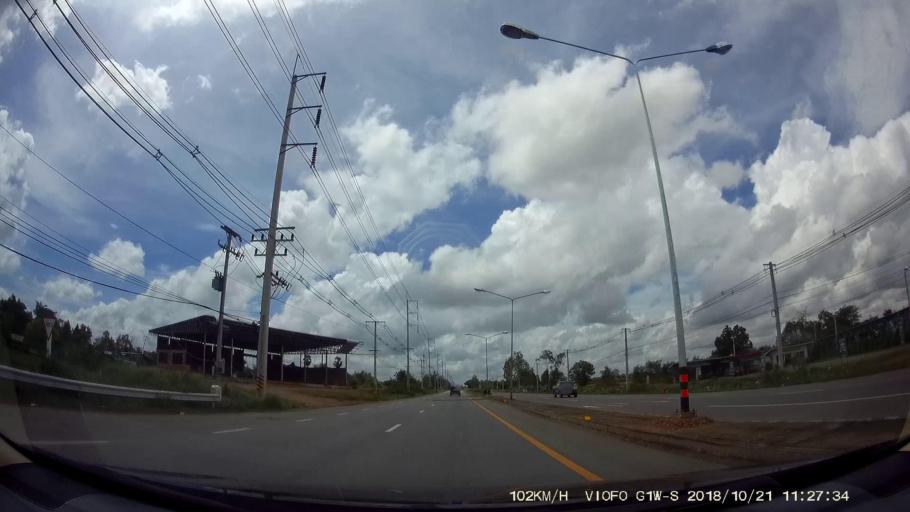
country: TH
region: Chaiyaphum
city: Chaiyaphum
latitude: 15.7989
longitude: 102.0551
